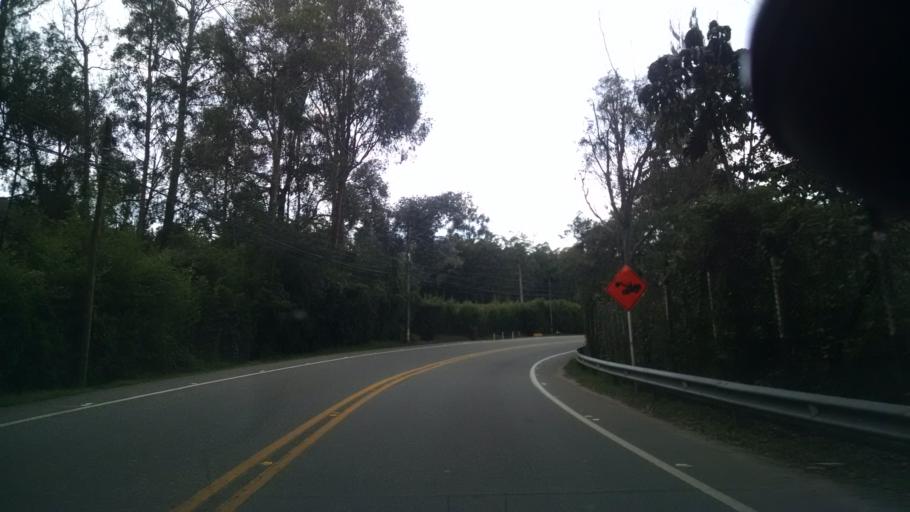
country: CO
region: Antioquia
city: El Retiro
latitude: 6.1059
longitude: -75.5024
